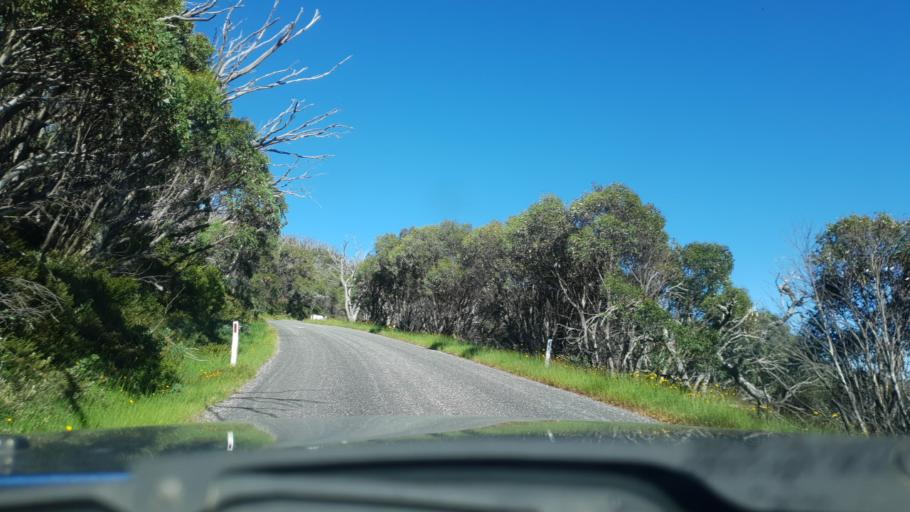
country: AU
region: Victoria
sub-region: Alpine
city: Mount Beauty
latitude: -36.8909
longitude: 147.3054
